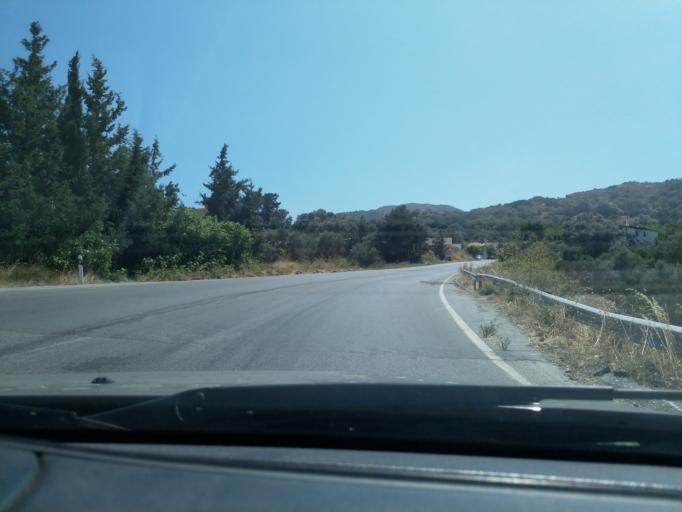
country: GR
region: Crete
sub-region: Nomos Rethymnis
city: Agia Foteini
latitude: 35.2211
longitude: 24.5002
